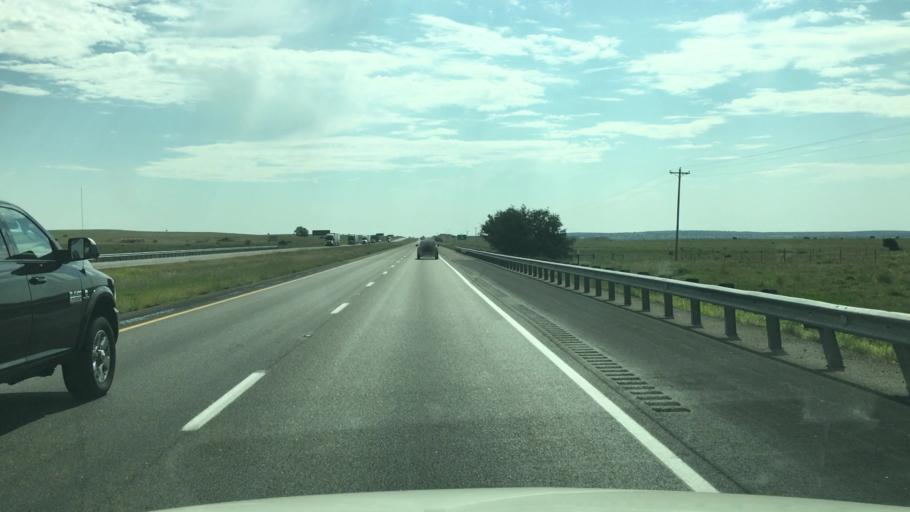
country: US
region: New Mexico
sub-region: San Miguel County
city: Las Vegas
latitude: 34.9910
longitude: -105.2882
